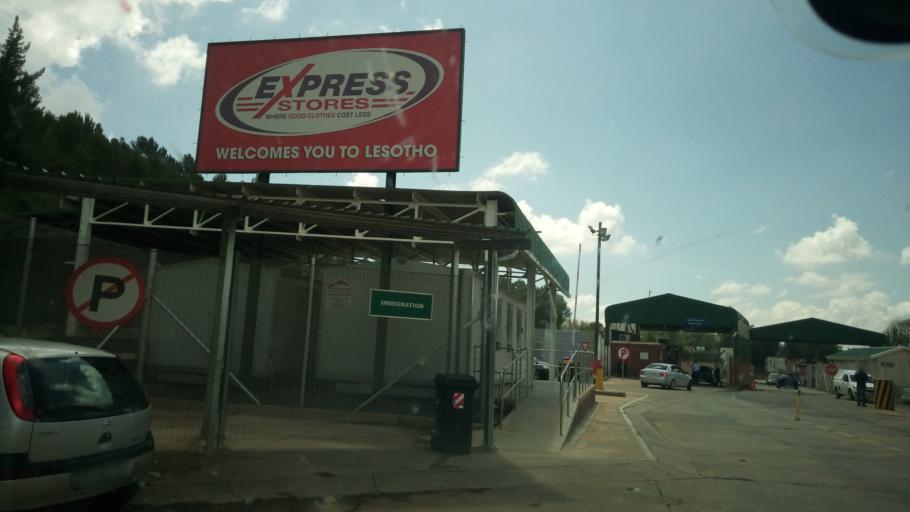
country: LS
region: Maseru
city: Maseru
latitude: -29.2975
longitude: 27.4523
